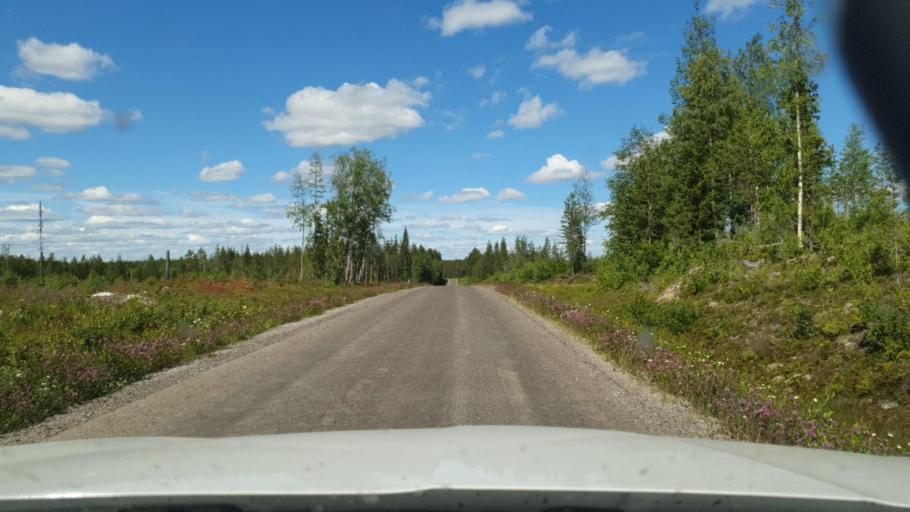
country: SE
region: Vaesterbotten
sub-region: Skelleftea Kommun
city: Byske
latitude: 65.1358
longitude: 21.1892
